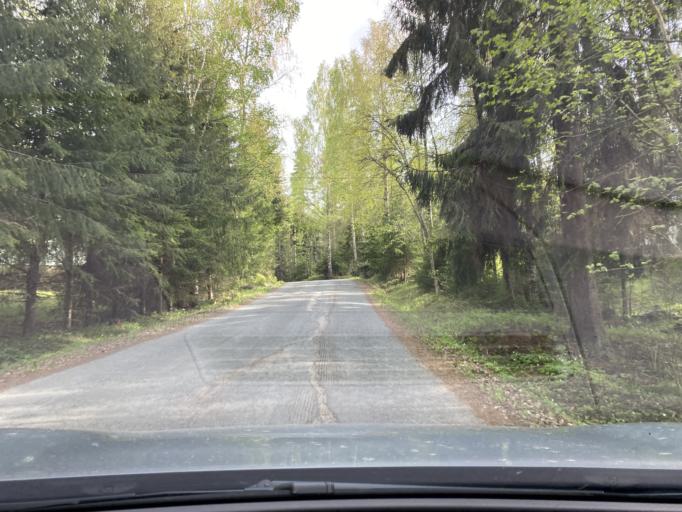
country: FI
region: Varsinais-Suomi
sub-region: Salo
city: Kiikala
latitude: 60.4520
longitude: 23.5526
